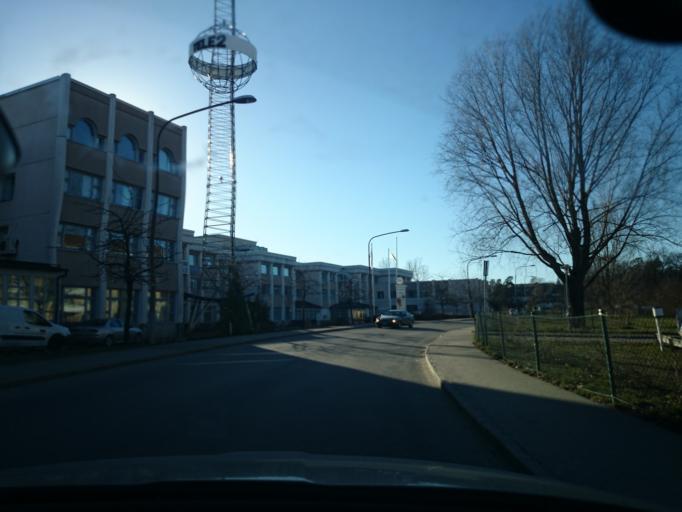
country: SE
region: Stockholm
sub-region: Huddinge Kommun
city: Segeltorp
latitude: 59.2894
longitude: 17.9513
